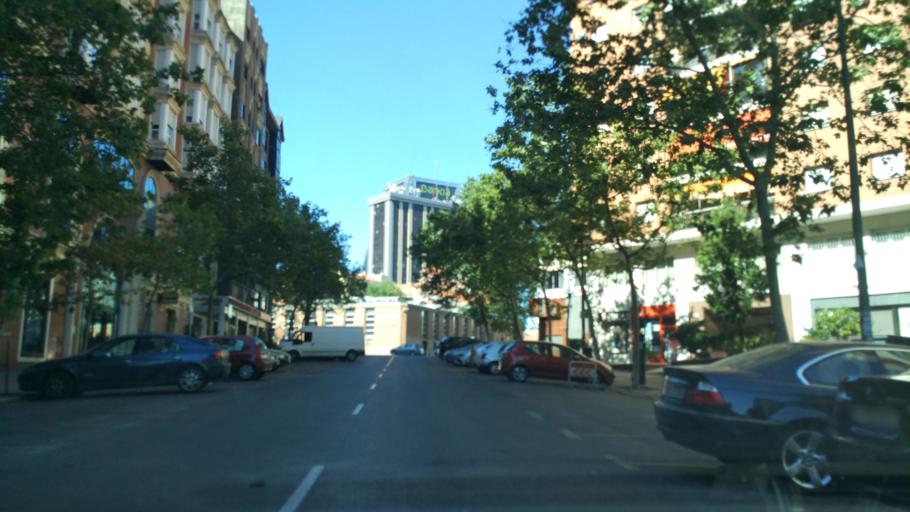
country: ES
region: Madrid
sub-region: Provincia de Madrid
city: Chamartin
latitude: 40.4636
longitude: -3.6933
